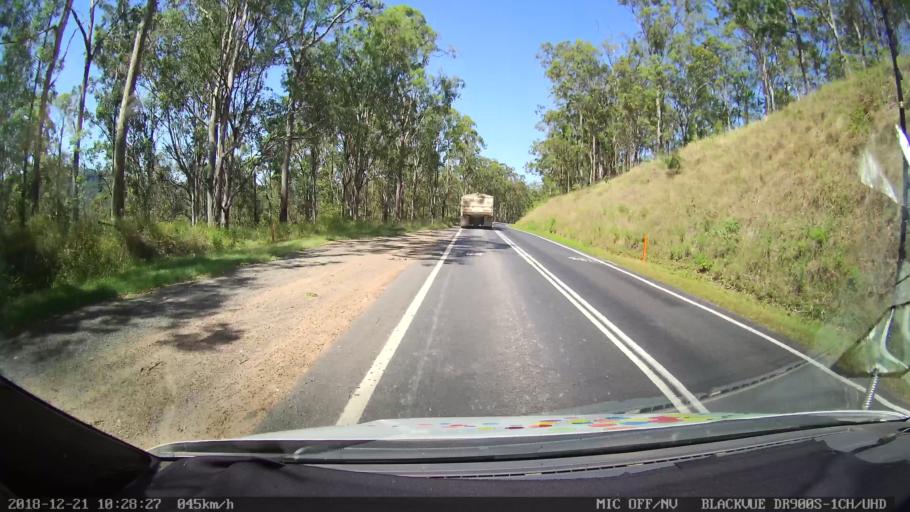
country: AU
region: New South Wales
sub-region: Clarence Valley
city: South Grafton
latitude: -29.6310
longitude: 152.7343
